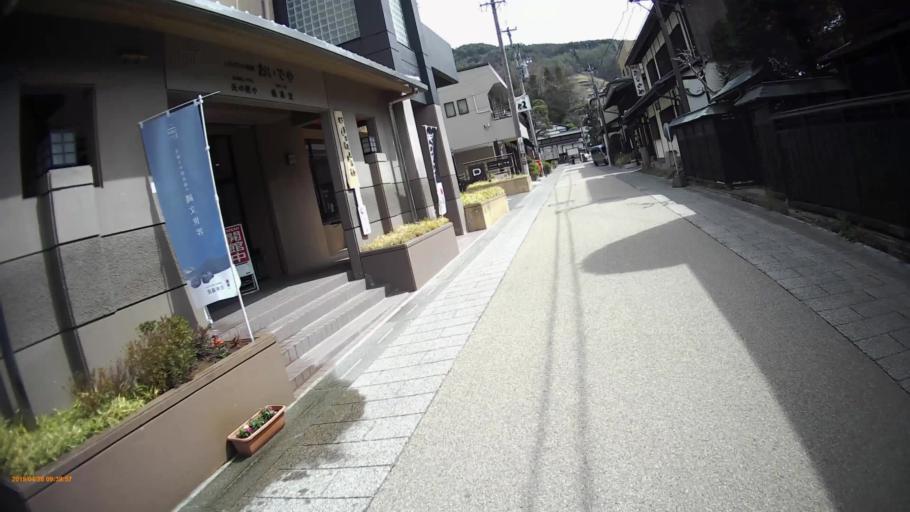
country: JP
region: Nagano
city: Suwa
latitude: 36.0755
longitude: 138.0894
